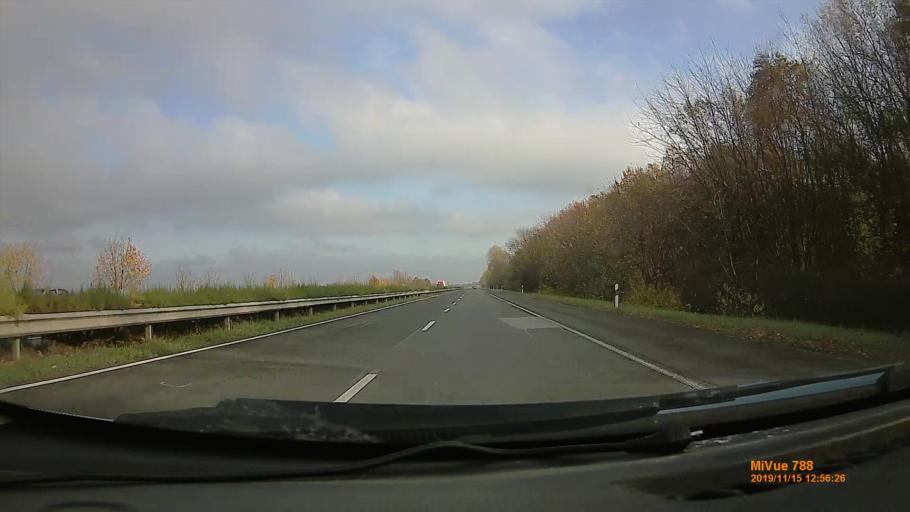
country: HU
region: Bekes
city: Bekescsaba
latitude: 46.6748
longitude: 21.1432
